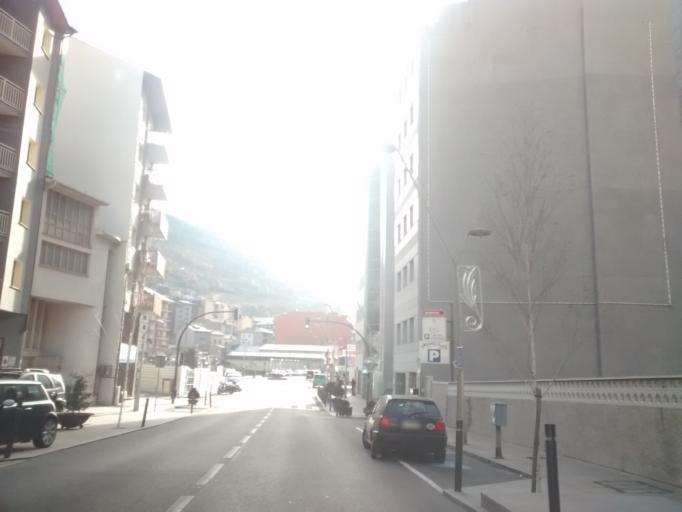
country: AD
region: Sant Julia de Loria
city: Sant Julia de Loria
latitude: 42.4694
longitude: 1.4928
